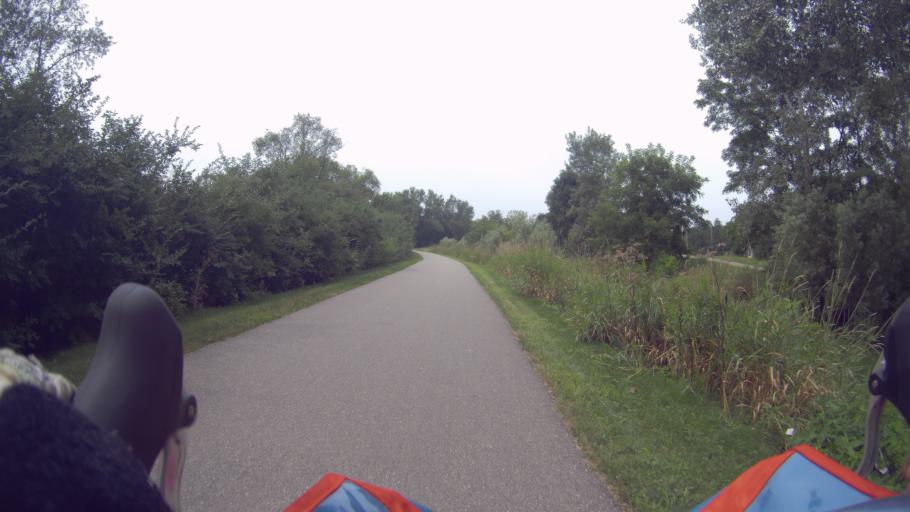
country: US
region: Wisconsin
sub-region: Dane County
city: Shorewood Hills
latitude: 43.0234
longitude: -89.4624
